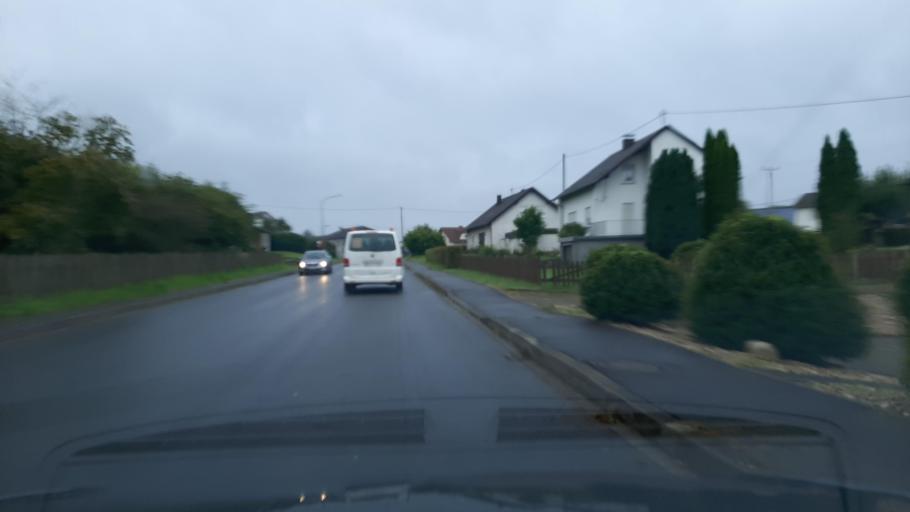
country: DE
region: Rheinland-Pfalz
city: Badem
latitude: 50.0041
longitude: 6.6070
